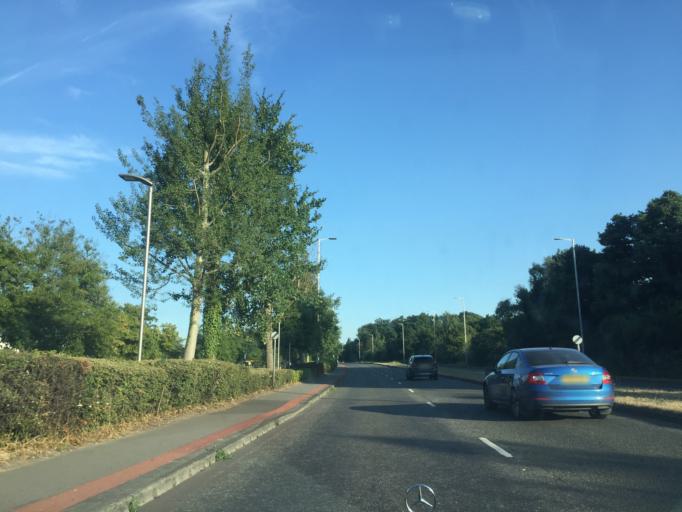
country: GB
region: England
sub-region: Bracknell Forest
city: Sandhurst
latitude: 51.3376
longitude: -0.7793
